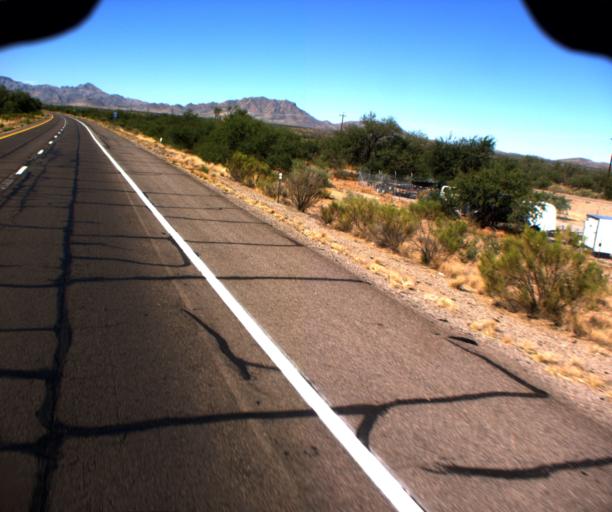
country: US
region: Arizona
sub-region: Pima County
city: Arivaca Junction
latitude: 31.7197
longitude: -111.0617
